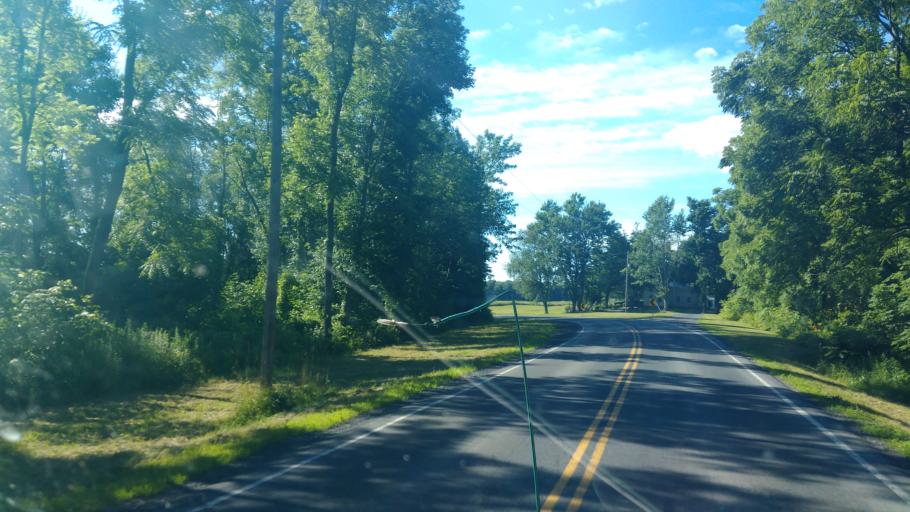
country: US
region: New York
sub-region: Wayne County
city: Clyde
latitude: 42.9994
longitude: -76.8726
